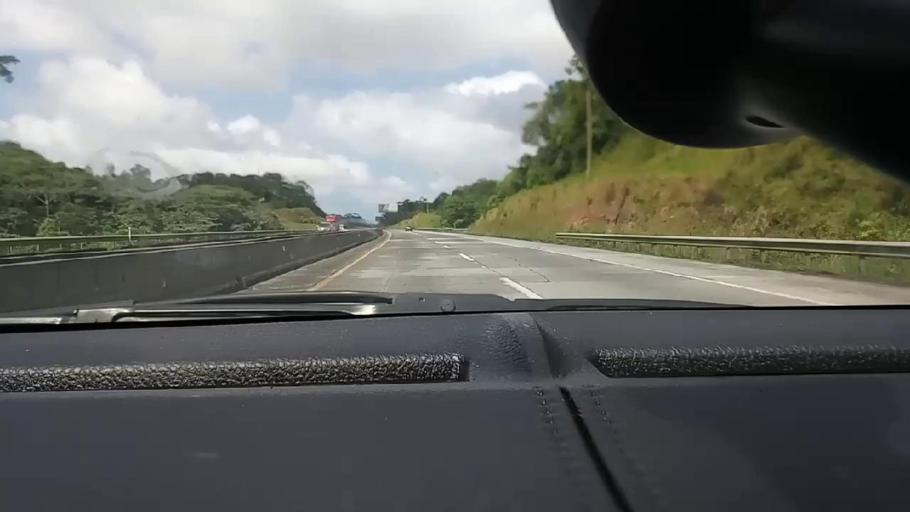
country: PA
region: Colon
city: Rio Rita
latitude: 9.2972
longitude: -79.7875
